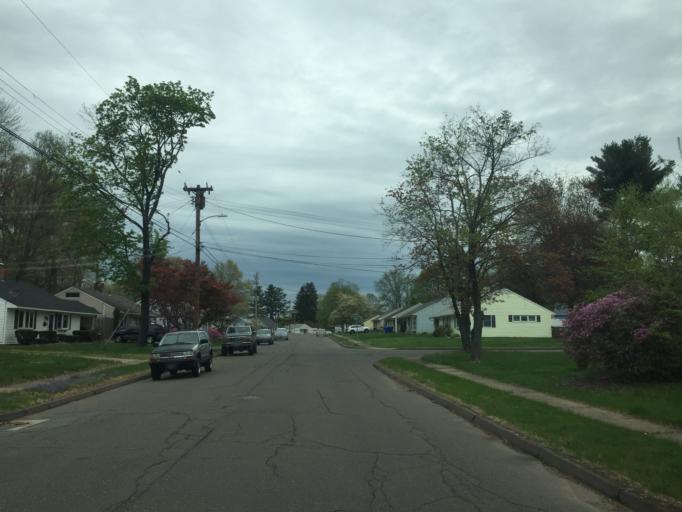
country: US
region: Connecticut
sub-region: Hartford County
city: Glastonbury
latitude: 41.7326
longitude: -72.5895
